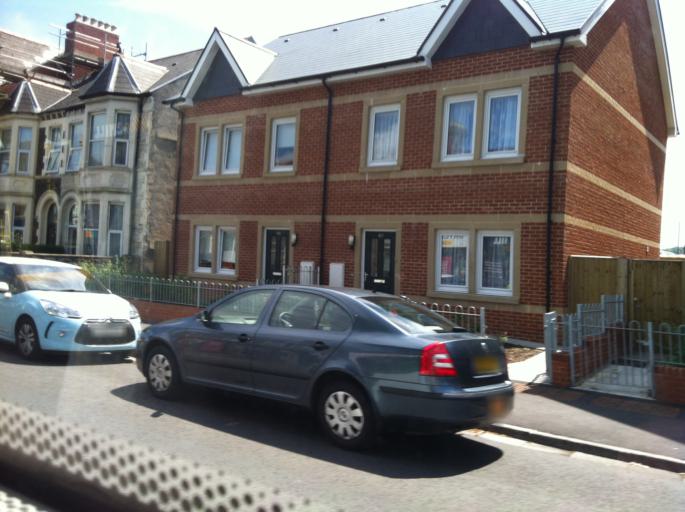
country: GB
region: Wales
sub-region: Cardiff
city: Cardiff
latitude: 51.4827
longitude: -3.2155
